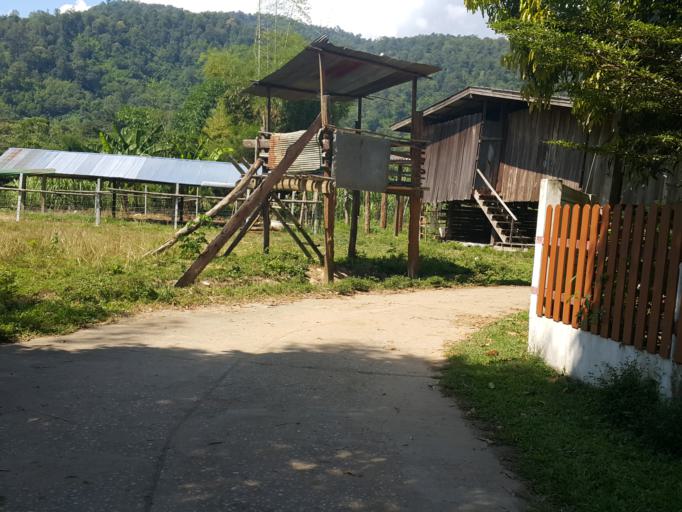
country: TH
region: Chiang Mai
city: Mae Taeng
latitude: 19.2022
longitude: 98.8859
